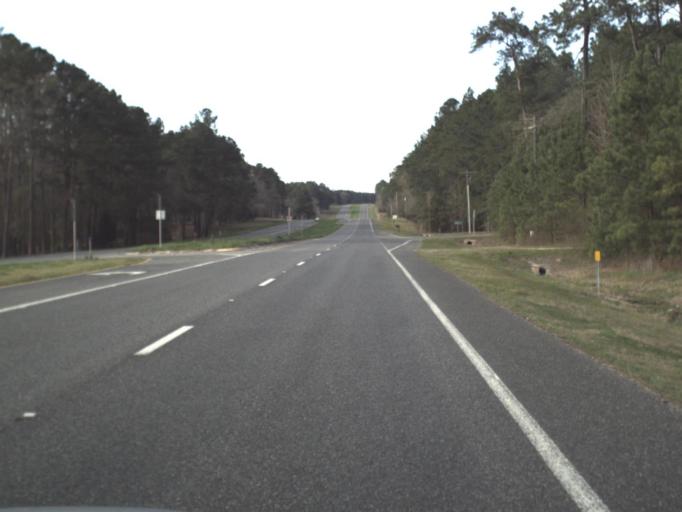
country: US
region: Florida
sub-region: Jefferson County
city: Monticello
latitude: 30.5938
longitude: -83.8706
